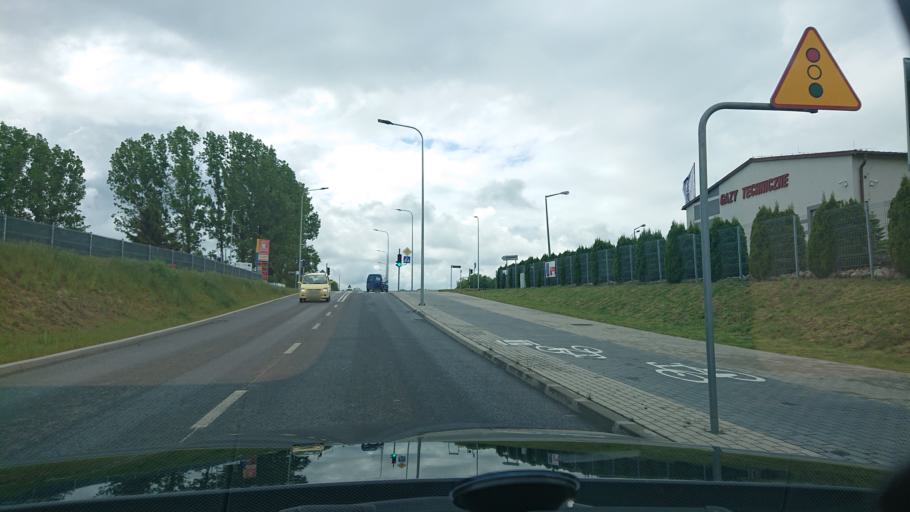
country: PL
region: Greater Poland Voivodeship
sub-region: Powiat gnieznienski
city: Gniezno
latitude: 52.5299
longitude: 17.6221
